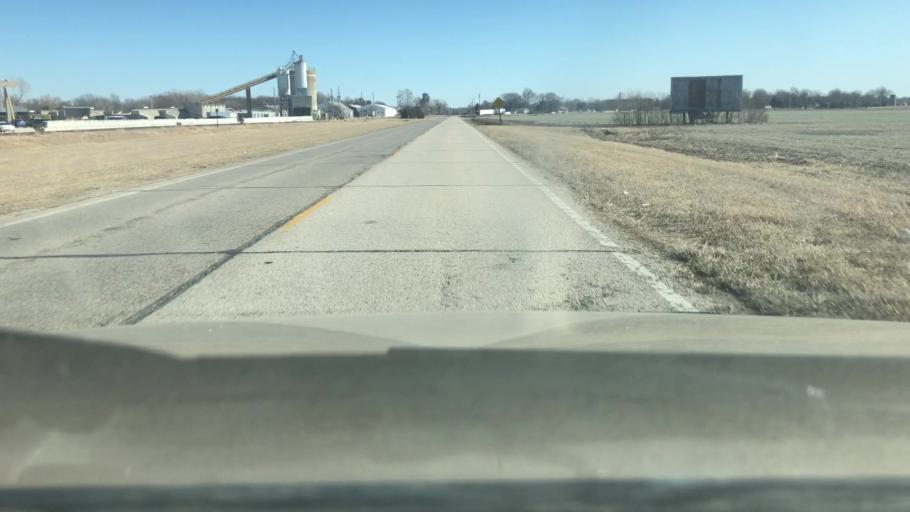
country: US
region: Kansas
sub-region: Harvey County
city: North Newton
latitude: 38.0763
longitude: -97.3593
